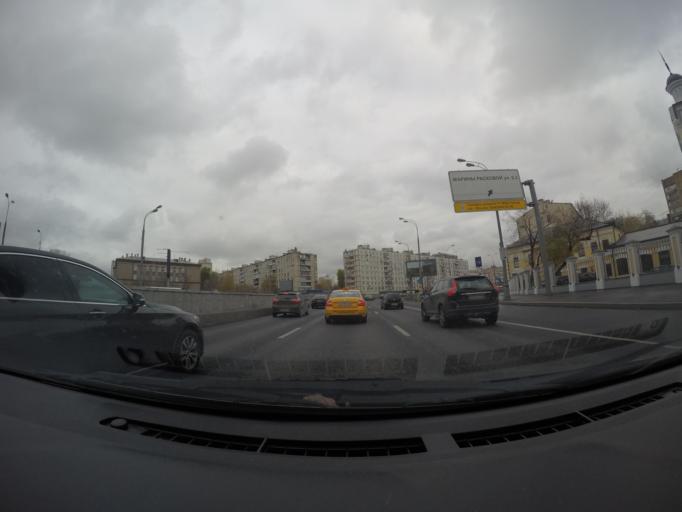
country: RU
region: Moskovskaya
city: Dorogomilovo
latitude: 55.7910
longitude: 37.5731
